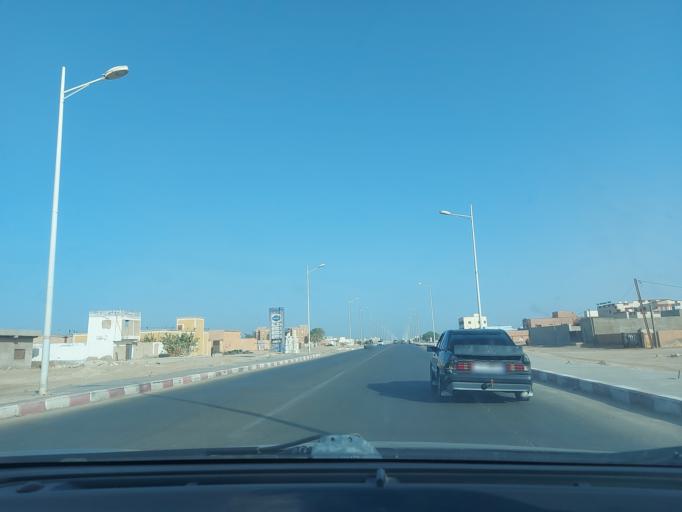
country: MR
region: Nouakchott
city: Nouakchott
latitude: 18.0885
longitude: -16.0058
